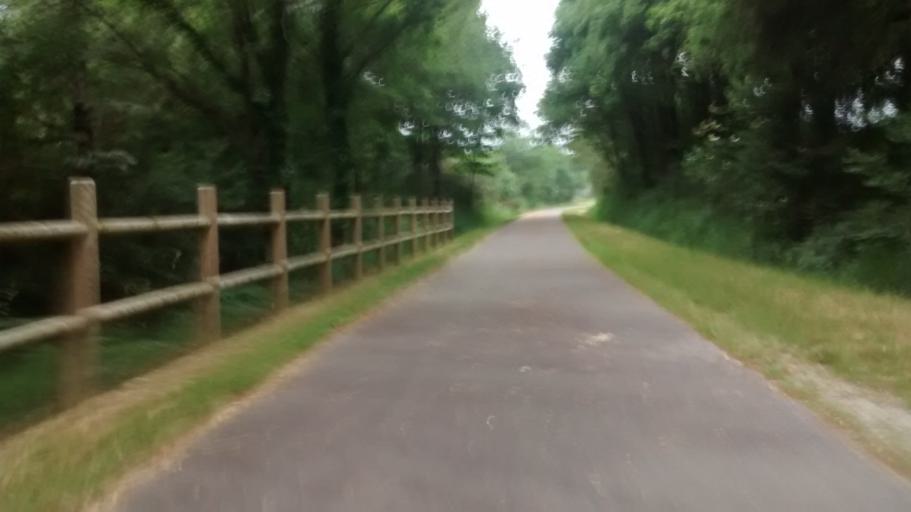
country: FR
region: Brittany
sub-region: Departement du Morbihan
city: Pleucadeuc
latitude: 47.7569
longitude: -2.4008
